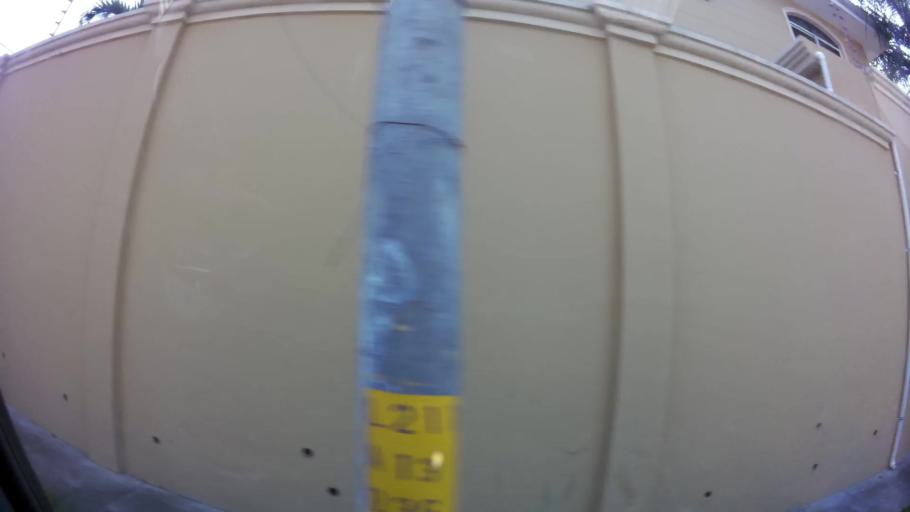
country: HN
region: Cortes
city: Armenta
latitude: 15.4954
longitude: -88.0406
